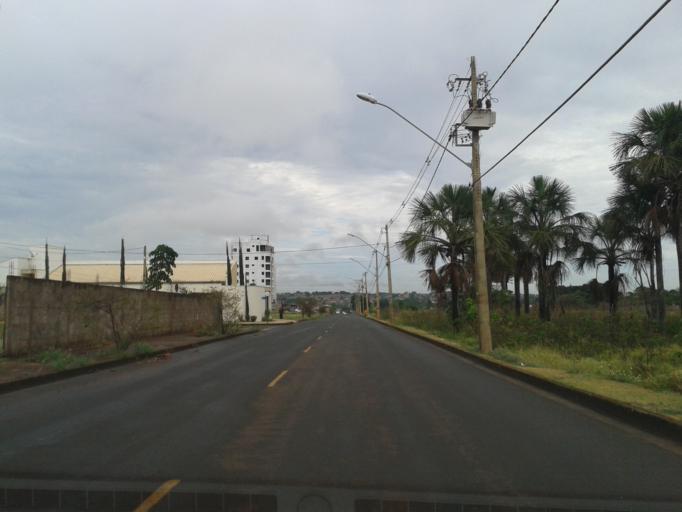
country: BR
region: Minas Gerais
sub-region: Ituiutaba
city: Ituiutaba
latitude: -19.0007
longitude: -49.4603
